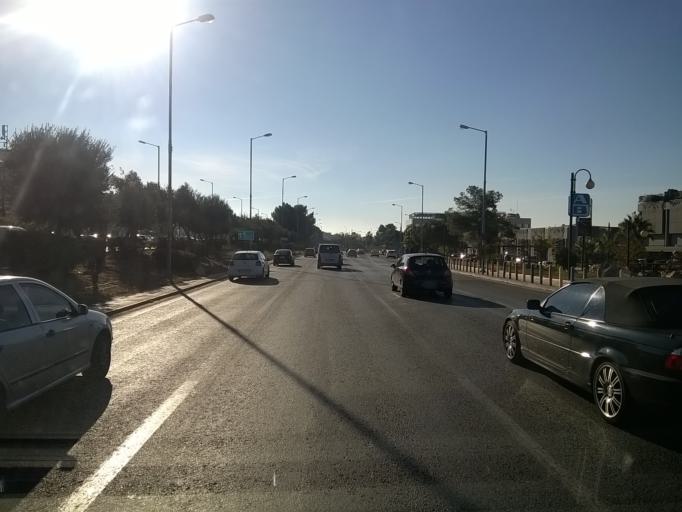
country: GR
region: Attica
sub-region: Nomarchia Athinas
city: Argyroupoli
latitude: 37.8917
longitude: 23.7479
